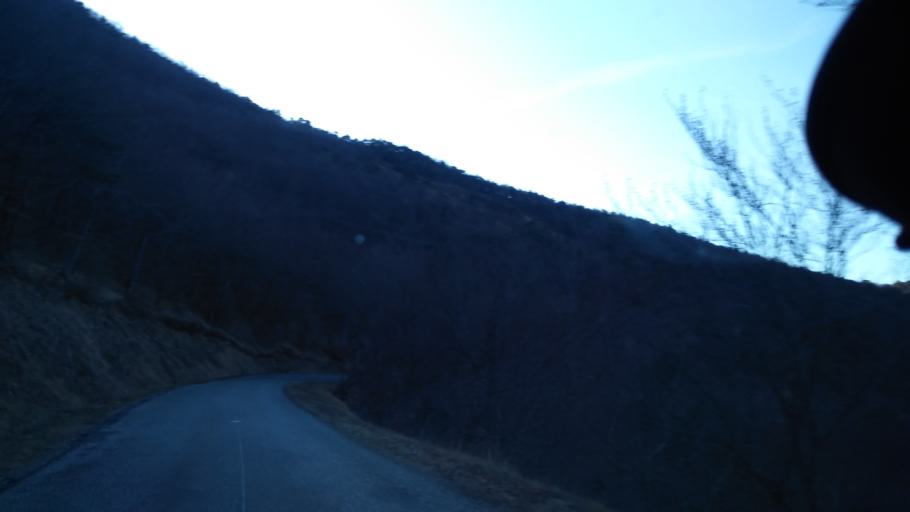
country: FR
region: Rhone-Alpes
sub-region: Departement de la Drome
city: Chabeuil
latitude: 44.8549
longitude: 5.0891
